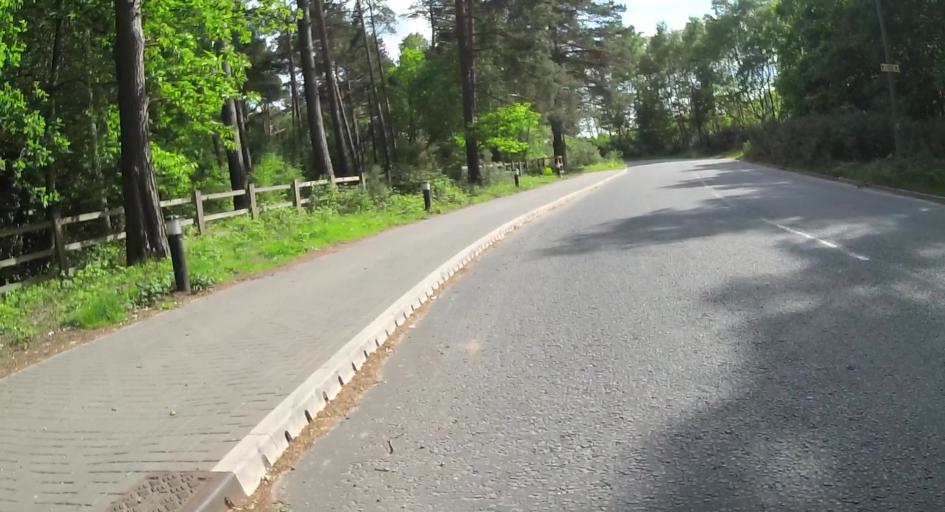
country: GB
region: England
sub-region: Hampshire
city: Fleet
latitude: 51.2873
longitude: -0.8040
